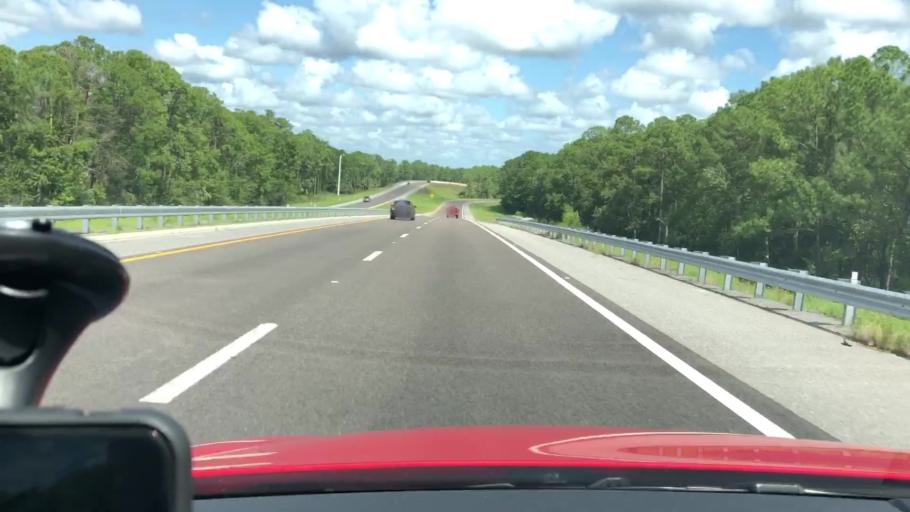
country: US
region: Florida
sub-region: Volusia County
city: Samsula-Spruce Creek
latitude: 29.1384
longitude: -81.1183
